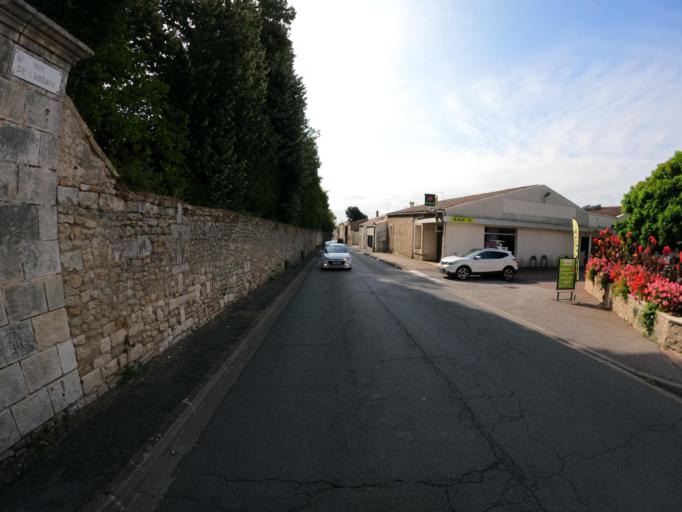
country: FR
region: Pays de la Loire
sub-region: Departement de la Vendee
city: Triaize
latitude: 46.3530
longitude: -1.2503
